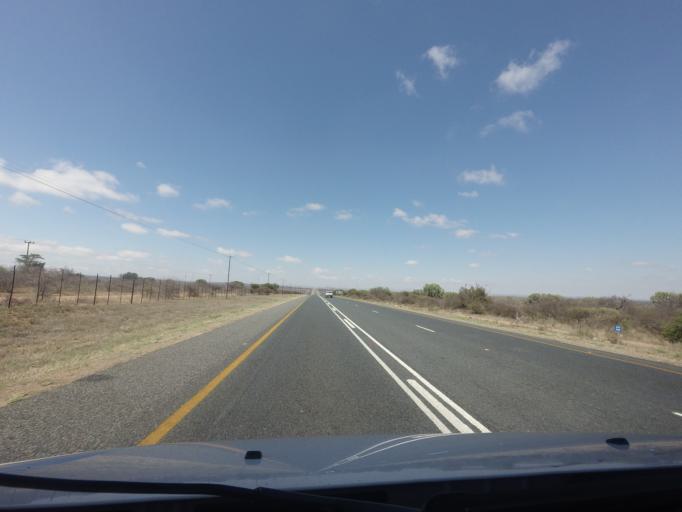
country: ZA
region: Limpopo
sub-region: Vhembe District Municipality
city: Louis Trichardt
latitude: -23.3760
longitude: 29.7687
